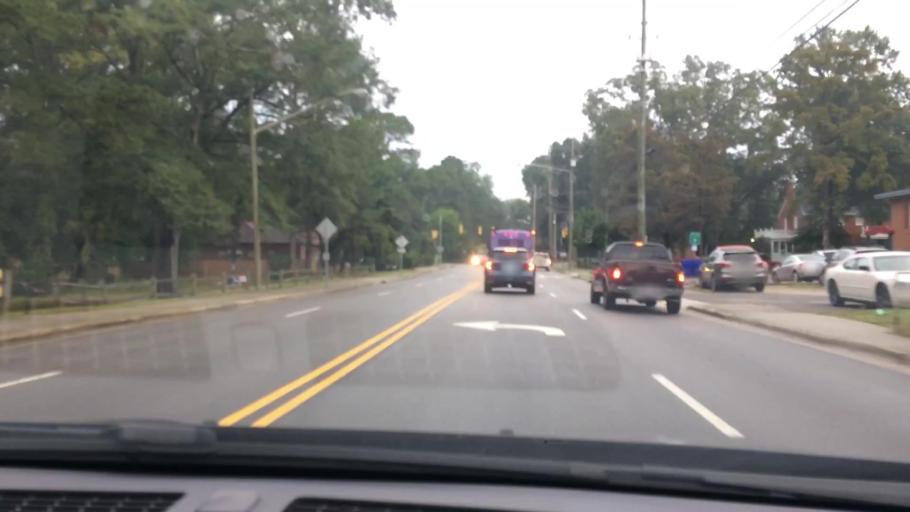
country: US
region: North Carolina
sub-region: Pitt County
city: Greenville
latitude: 35.6022
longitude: -77.3589
